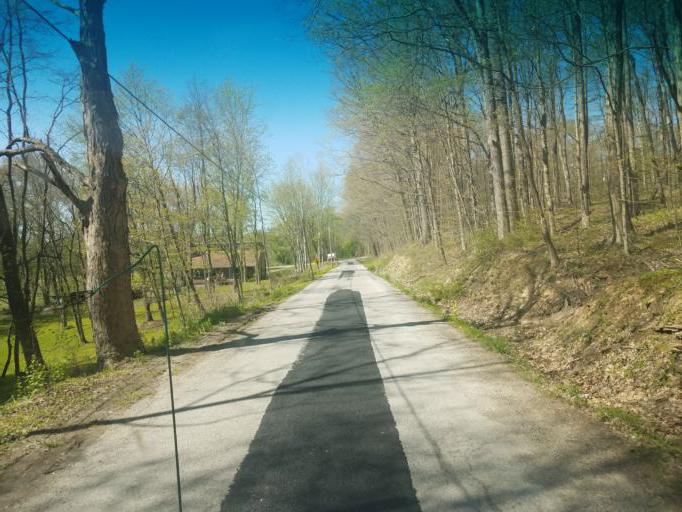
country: US
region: Ohio
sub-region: Medina County
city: Lodi
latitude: 40.9728
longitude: -82.0253
